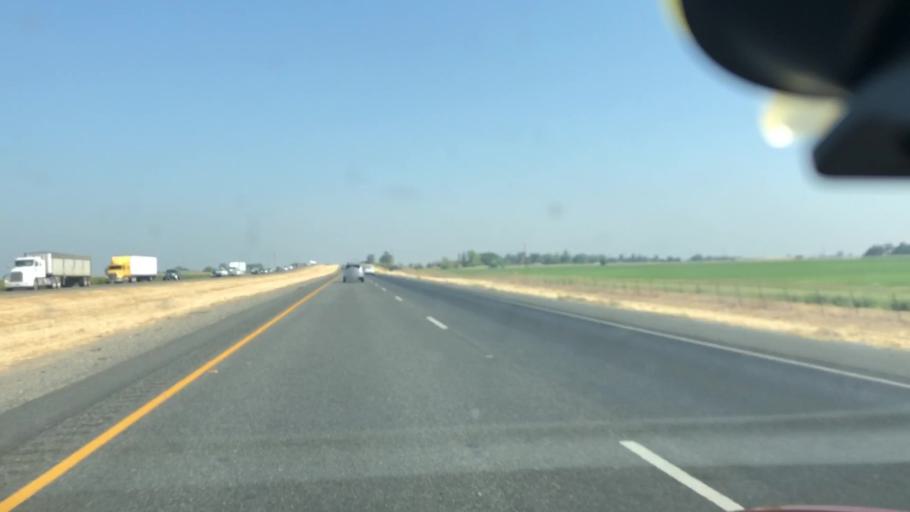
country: US
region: California
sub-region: Sacramento County
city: Walnut Grove
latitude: 38.3134
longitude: -121.4638
